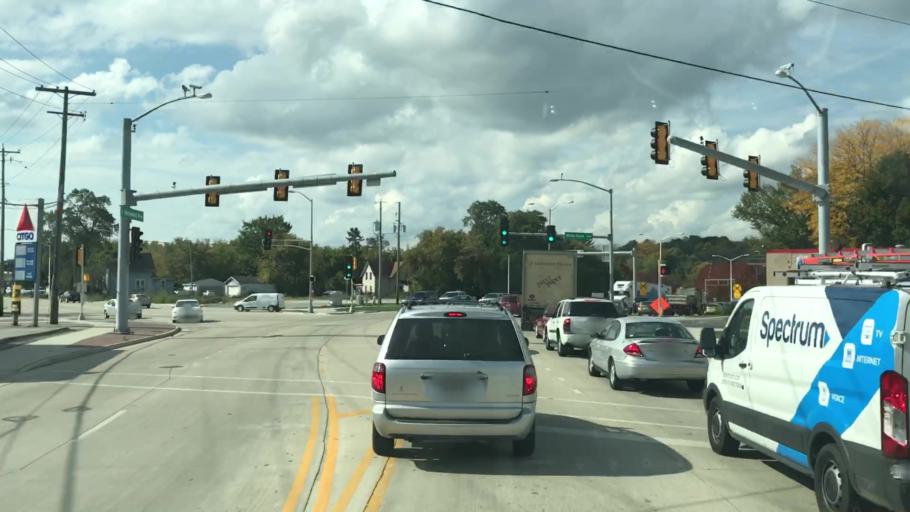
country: US
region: Wisconsin
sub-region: Waukesha County
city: Waukesha
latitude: 43.0221
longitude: -88.2180
